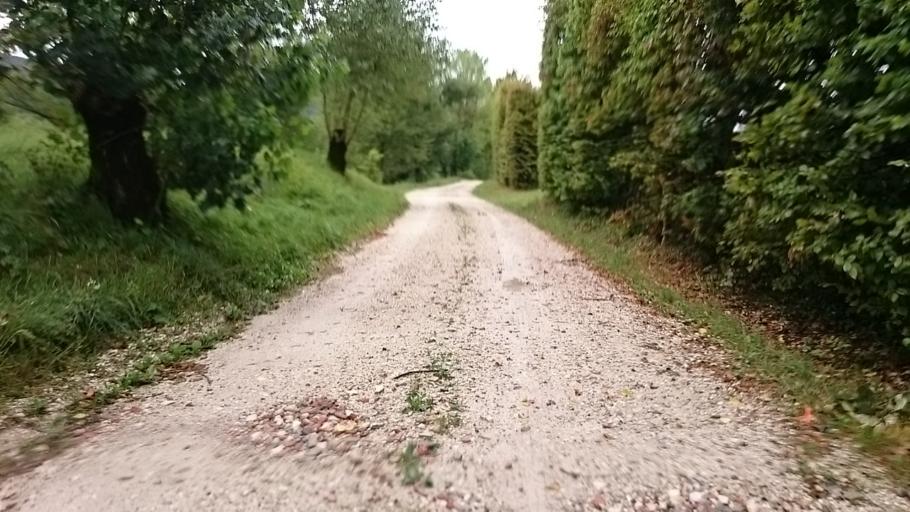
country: IT
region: Veneto
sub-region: Provincia di Treviso
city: Monfumo
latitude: 45.8224
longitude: 11.9173
